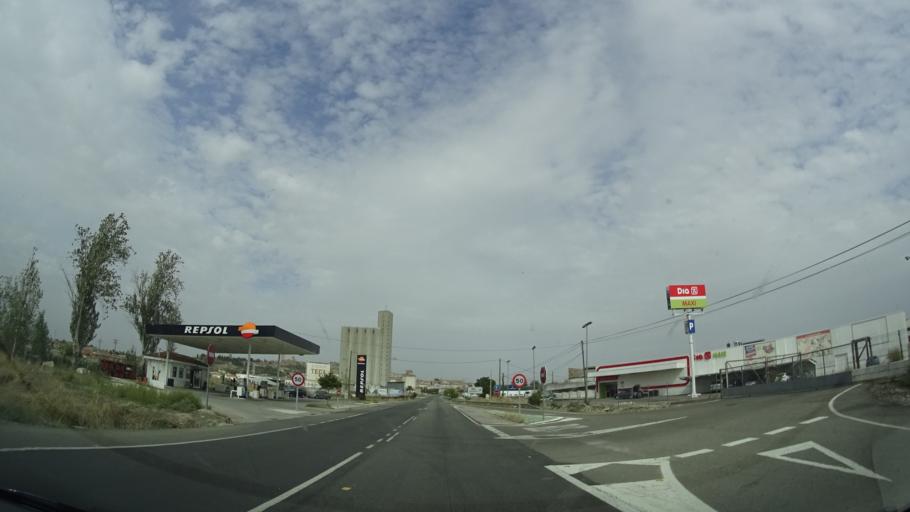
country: ES
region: Extremadura
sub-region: Provincia de Caceres
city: Trujillo
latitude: 39.4485
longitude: -5.8813
